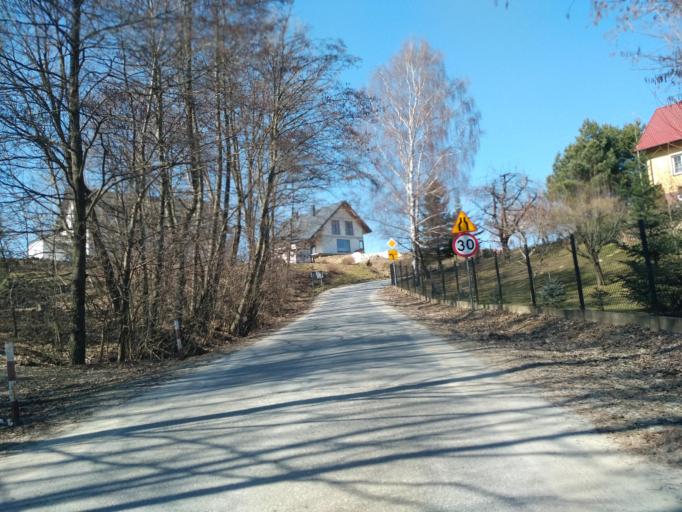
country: PL
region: Subcarpathian Voivodeship
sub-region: Powiat rzeszowski
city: Niechobrz
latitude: 49.9743
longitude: 21.8561
